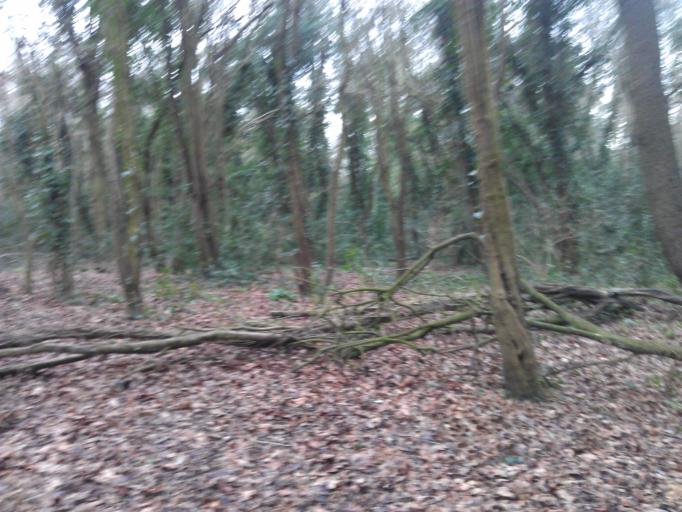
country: GB
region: England
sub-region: Essex
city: Wivenhoe
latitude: 51.8583
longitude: 0.9547
